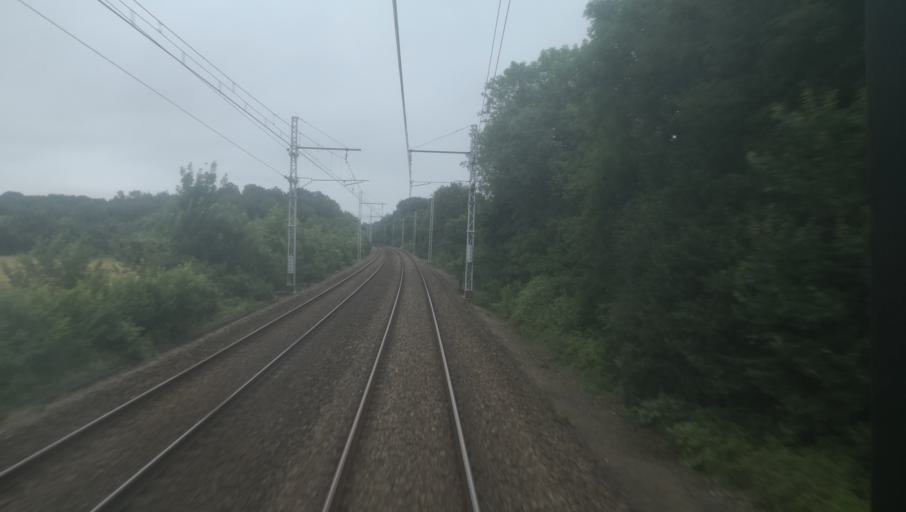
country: FR
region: Centre
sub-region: Departement de l'Indre
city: Luant
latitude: 46.6690
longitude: 1.5418
